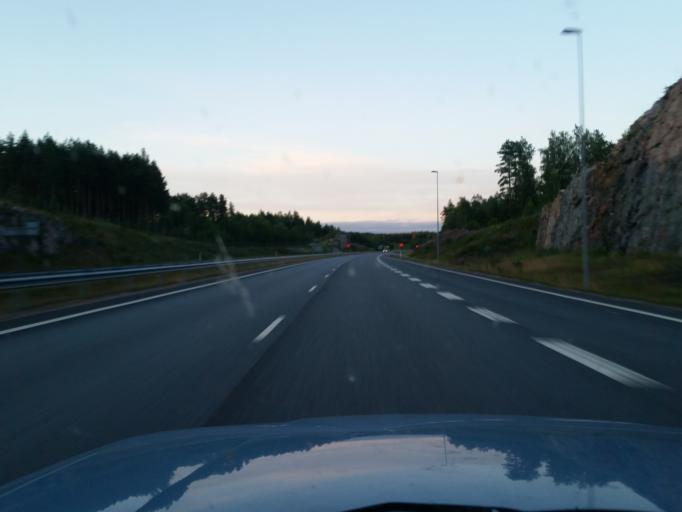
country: FI
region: Varsinais-Suomi
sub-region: Salo
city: Suomusjaervi
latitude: 60.3736
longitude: 23.7155
